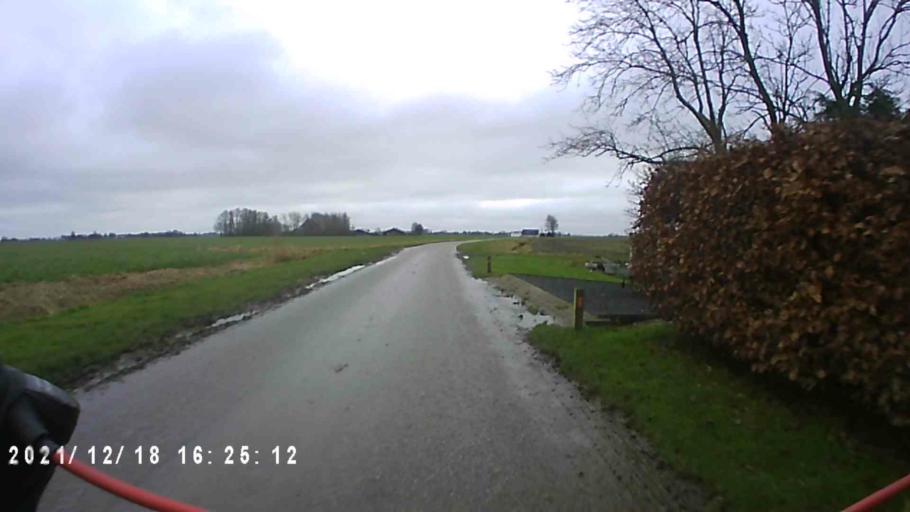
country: NL
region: Friesland
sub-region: Gemeente Dongeradeel
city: Dokkum
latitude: 53.3775
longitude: 6.0361
